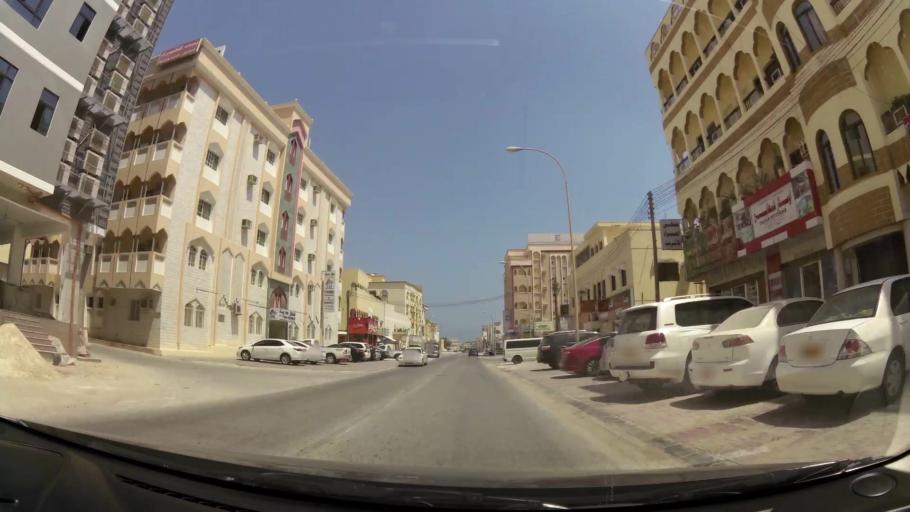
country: OM
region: Zufar
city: Salalah
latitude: 17.0156
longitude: 54.0806
